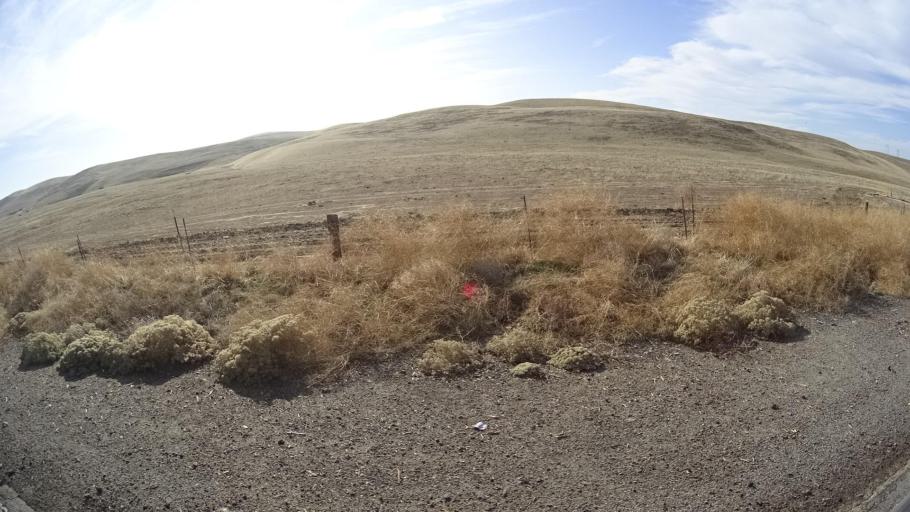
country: US
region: California
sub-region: Tulare County
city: Richgrove
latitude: 35.6212
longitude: -119.0318
